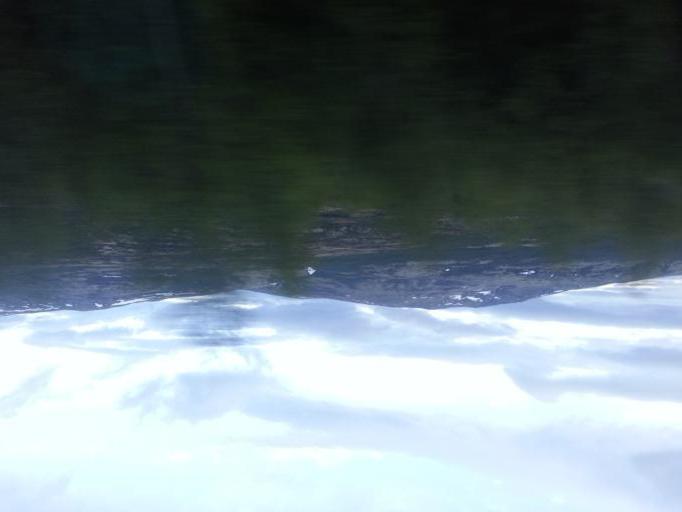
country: NO
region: Oppland
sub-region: Dovre
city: Dovre
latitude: 62.2020
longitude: 9.5291
